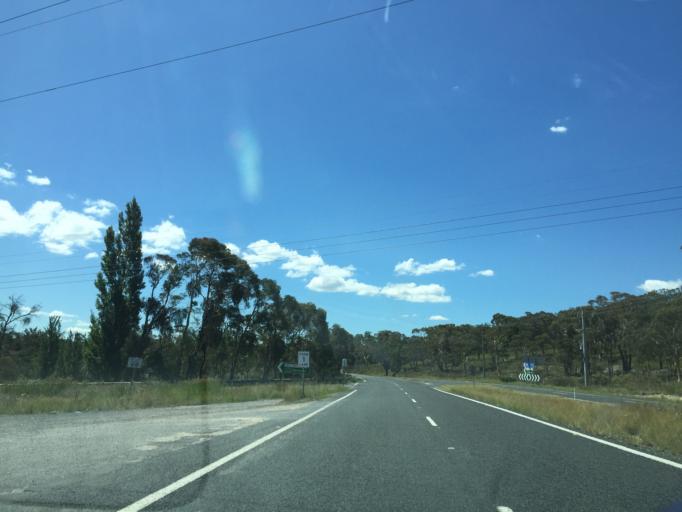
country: AU
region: New South Wales
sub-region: Lithgow
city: Lithgow
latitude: -33.4258
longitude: 150.1043
